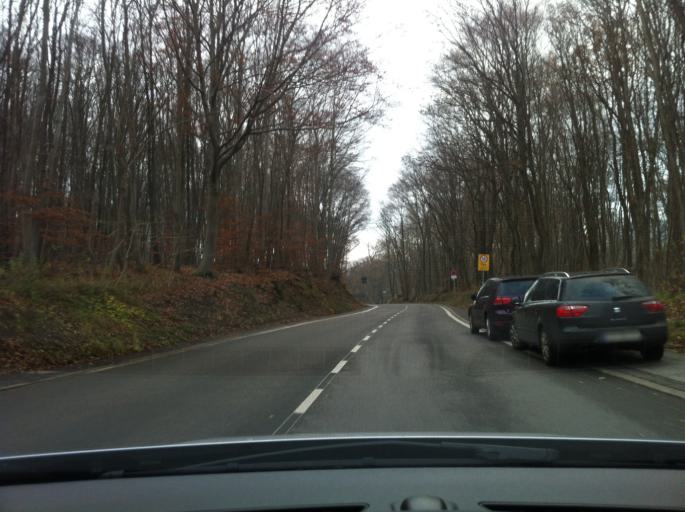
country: AT
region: Lower Austria
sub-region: Politischer Bezirk Wien-Umgebung
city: Klosterneuburg
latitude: 48.2405
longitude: 16.2755
